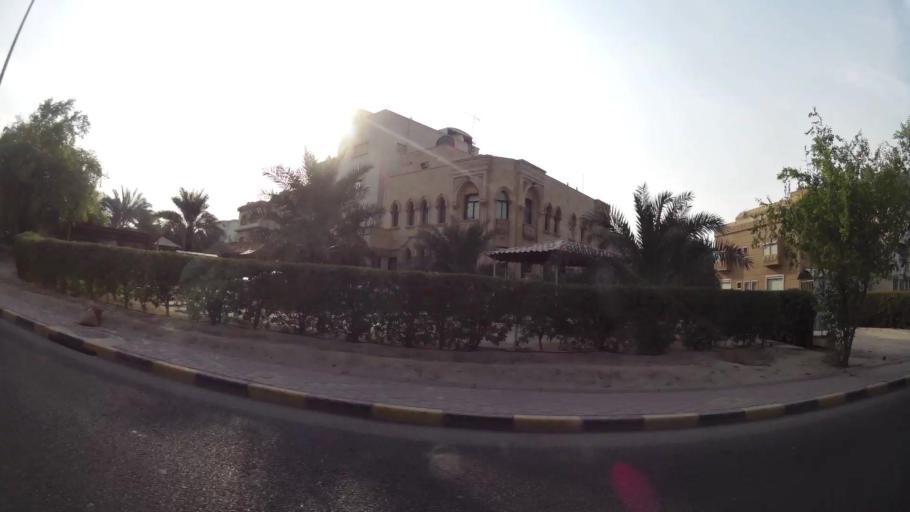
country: KW
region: Mubarak al Kabir
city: Mubarak al Kabir
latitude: 29.2093
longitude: 48.0686
